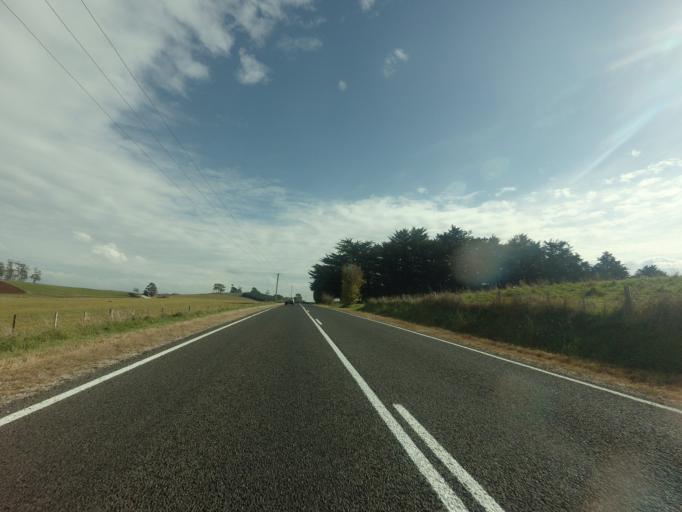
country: AU
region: Tasmania
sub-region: Meander Valley
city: Deloraine
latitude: -41.5254
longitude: 146.6984
